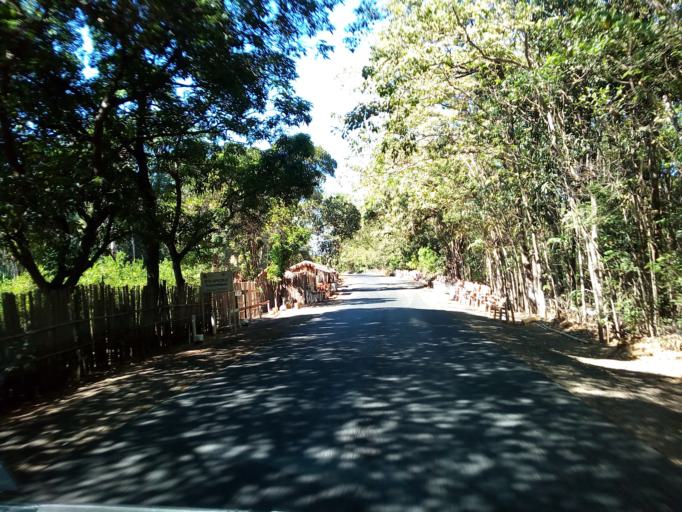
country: MG
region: Boeny
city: Ambato Boeny
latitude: -16.2755
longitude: 46.8110
